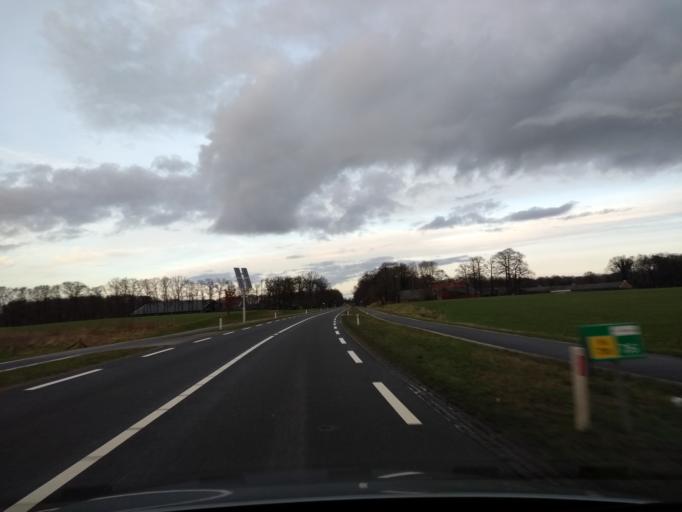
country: NL
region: Overijssel
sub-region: Gemeente Oldenzaal
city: Oldenzaal
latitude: 52.3268
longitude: 6.8546
